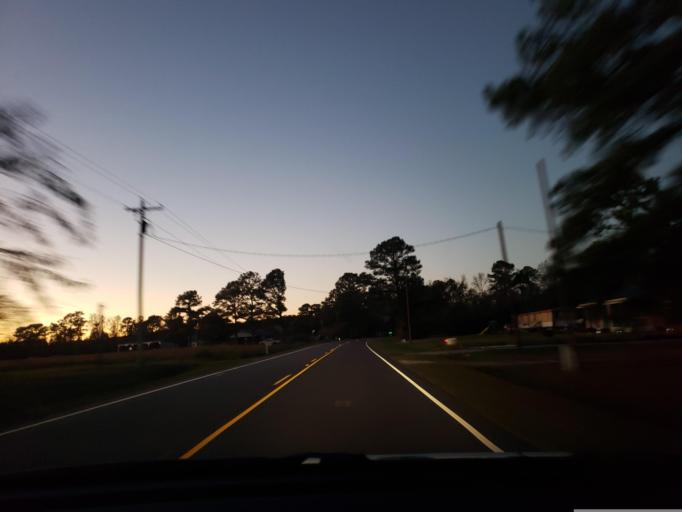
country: US
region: North Carolina
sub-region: Duplin County
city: Kenansville
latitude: 34.9238
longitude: -77.9362
